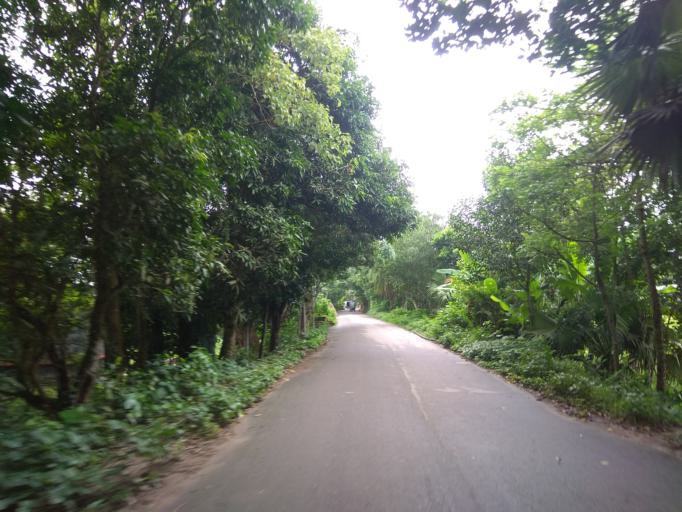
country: BD
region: Dhaka
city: Dohar
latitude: 23.4469
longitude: 90.0624
